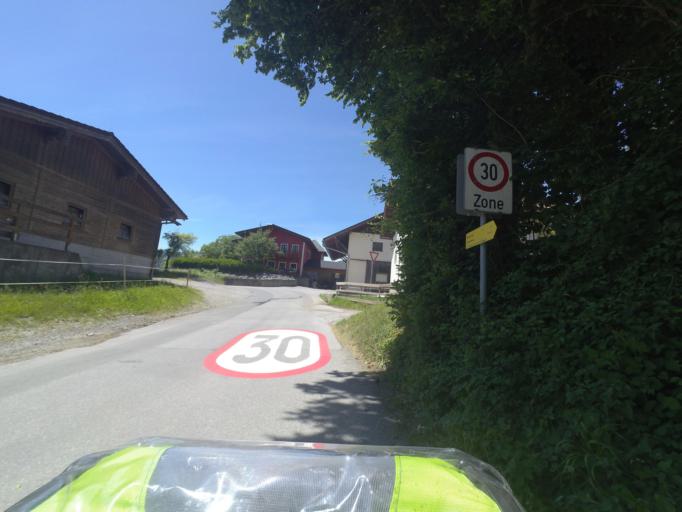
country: AT
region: Salzburg
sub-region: Politischer Bezirk Hallein
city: Oberalm
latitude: 47.7022
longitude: 13.1109
